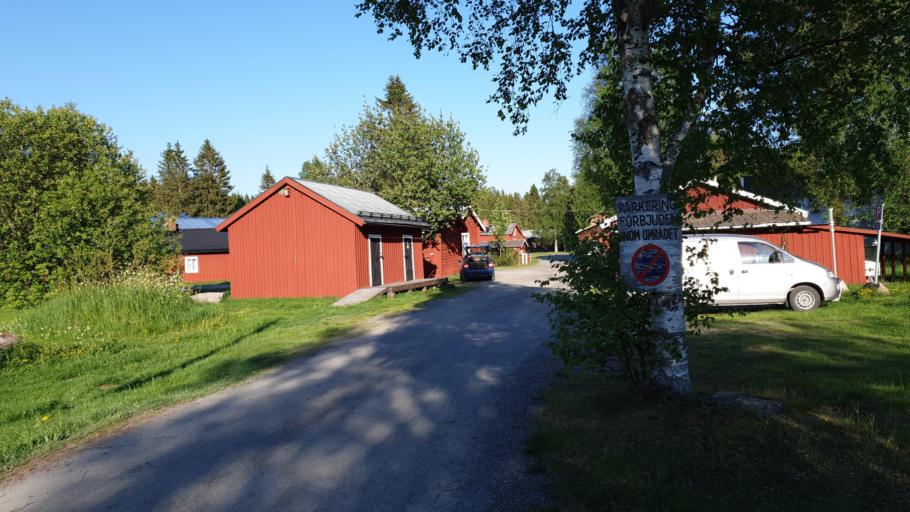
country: SE
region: Norrbotten
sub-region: Lulea Kommun
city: Gammelstad
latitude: 65.6490
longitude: 22.0343
